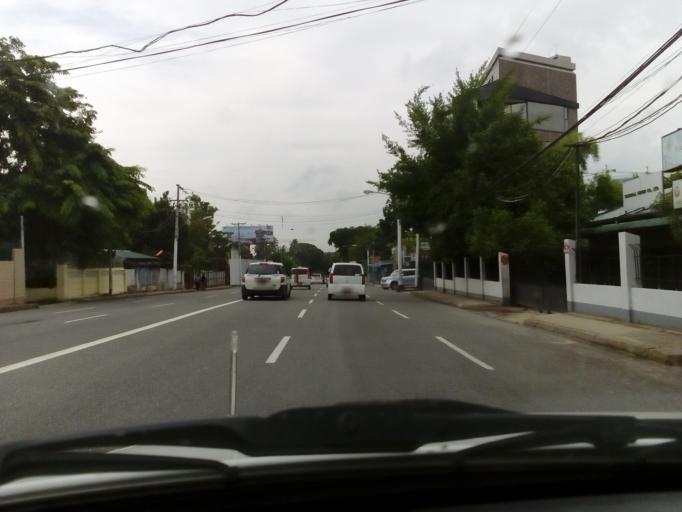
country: MM
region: Yangon
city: Yangon
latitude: 16.8200
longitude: 96.1557
